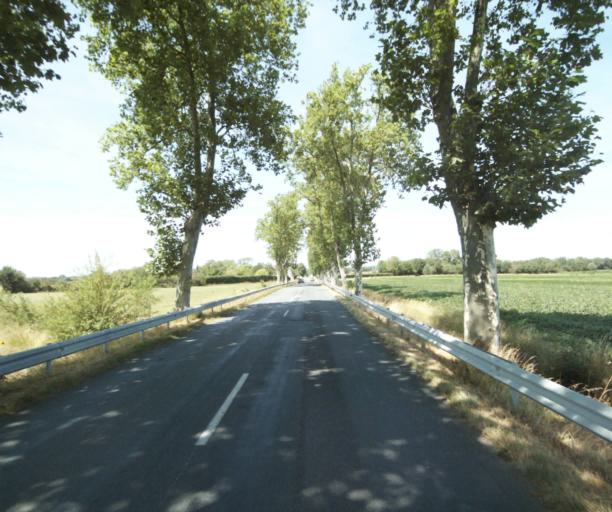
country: FR
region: Midi-Pyrenees
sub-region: Departement de la Haute-Garonne
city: Revel
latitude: 43.5098
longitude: 2.0108
